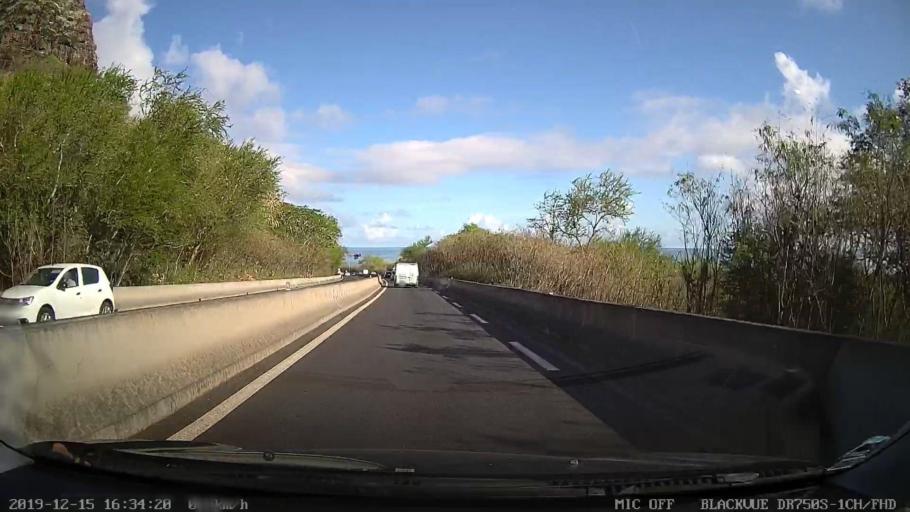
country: RE
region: Reunion
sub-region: Reunion
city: Saint-Denis
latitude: -20.8800
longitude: 55.4386
